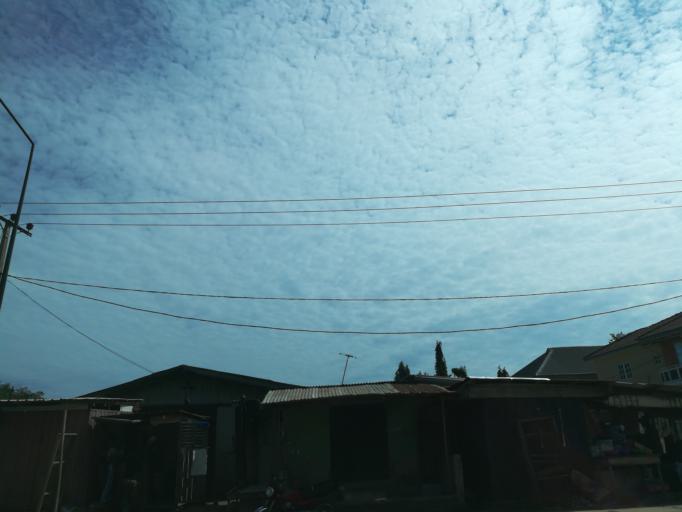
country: NG
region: Lagos
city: Ebute Ikorodu
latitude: 6.5968
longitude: 3.5019
